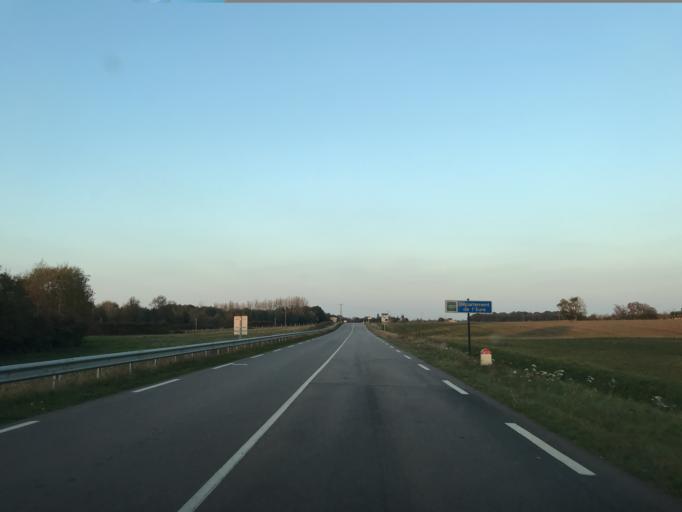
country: FR
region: Haute-Normandie
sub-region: Departement de l'Eure
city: Bourth
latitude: 48.6764
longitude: 0.7963
